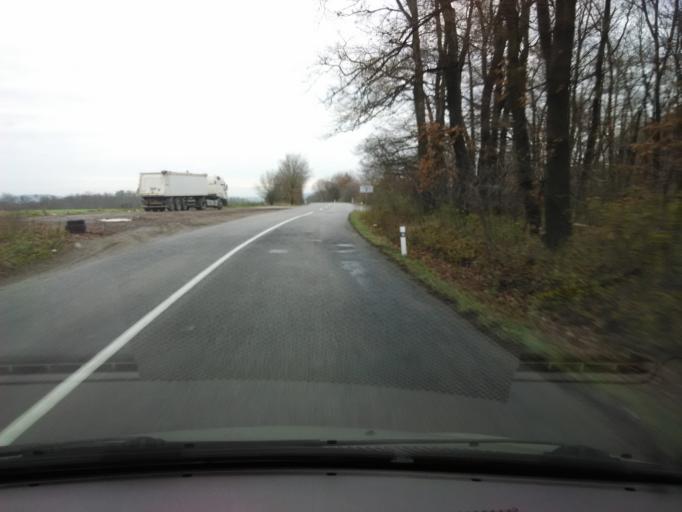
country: SK
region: Nitriansky
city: Tlmace
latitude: 48.3471
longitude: 18.4837
